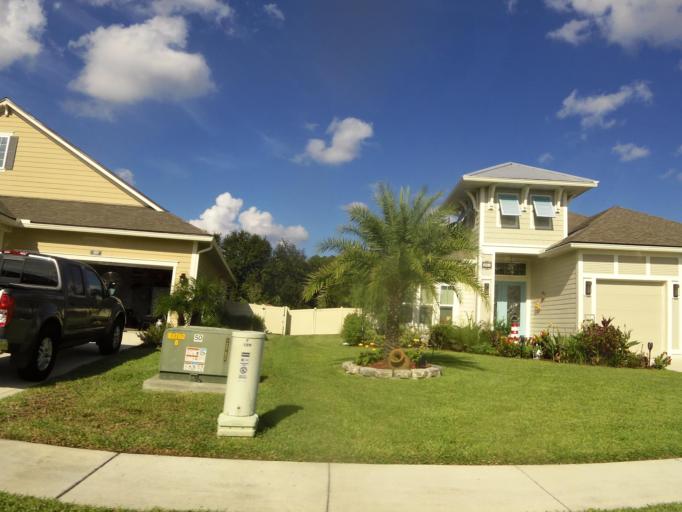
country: US
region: Florida
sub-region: Saint Johns County
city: Saint Augustine
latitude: 29.9286
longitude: -81.4916
